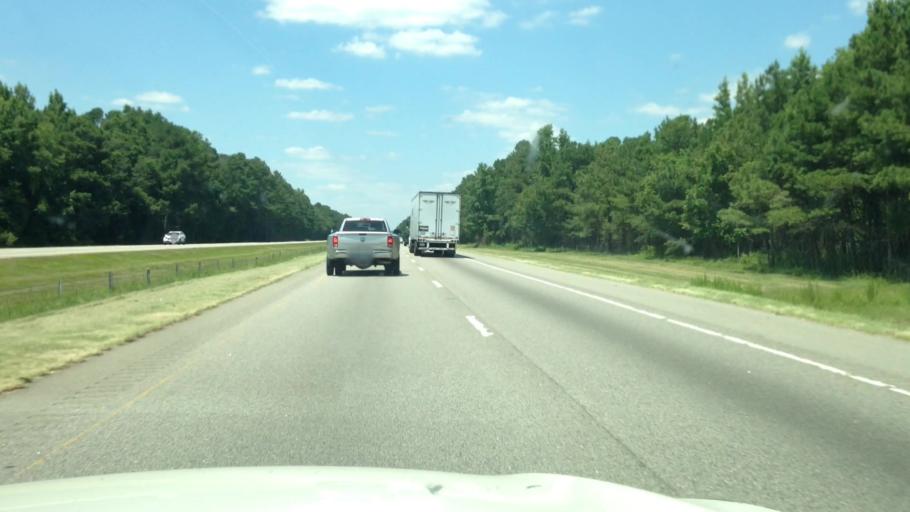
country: US
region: North Carolina
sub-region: Robeson County
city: Saint Pauls
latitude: 34.7714
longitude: -78.9960
